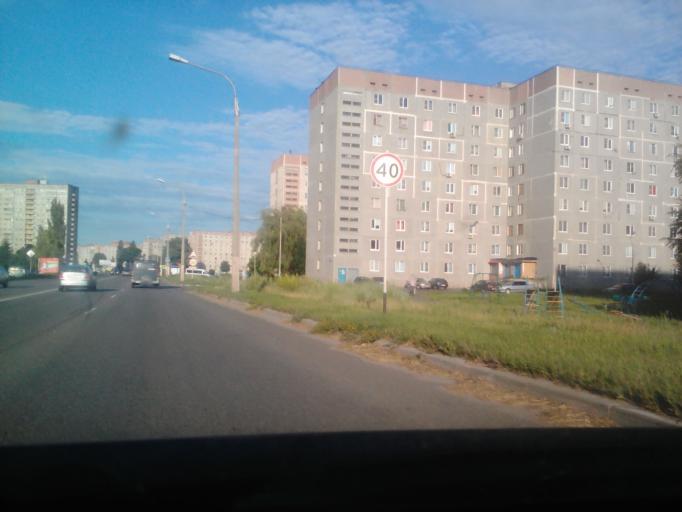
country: RU
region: Kursk
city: Kurchatov
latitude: 51.6531
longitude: 35.6777
